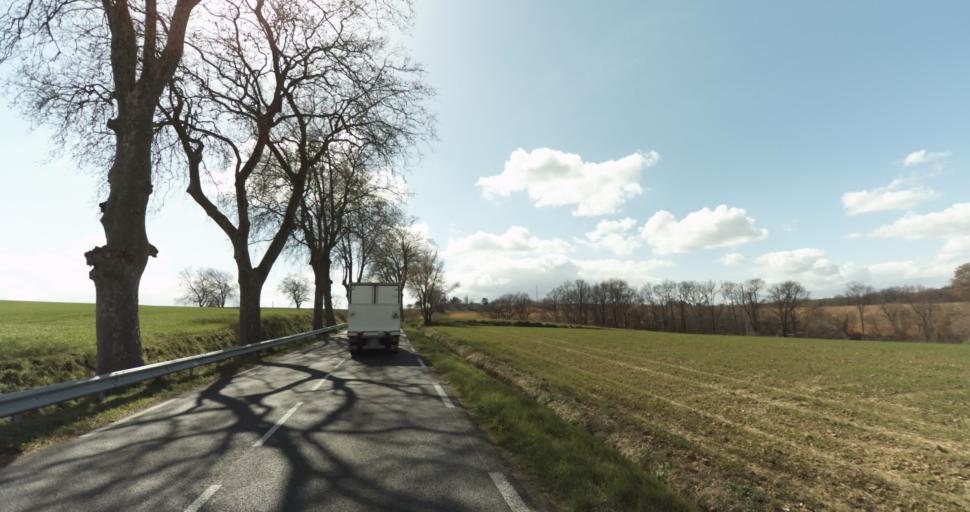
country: FR
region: Midi-Pyrenees
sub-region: Departement de la Haute-Garonne
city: Auterive
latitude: 43.3608
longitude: 1.5250
